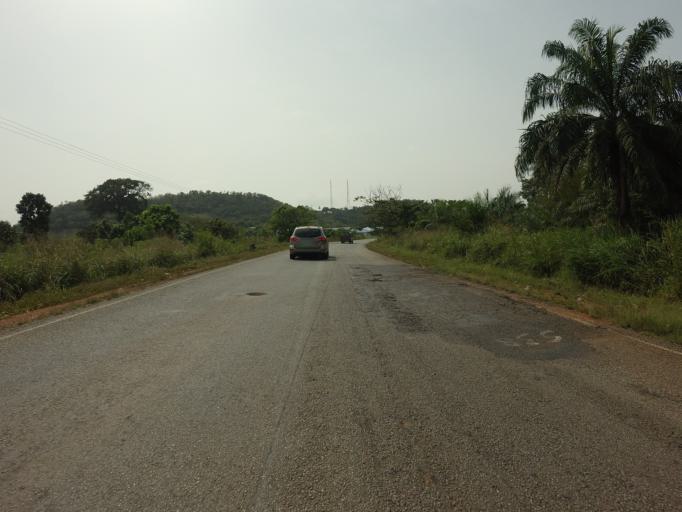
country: GH
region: Volta
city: Ho
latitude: 6.3469
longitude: 0.1748
